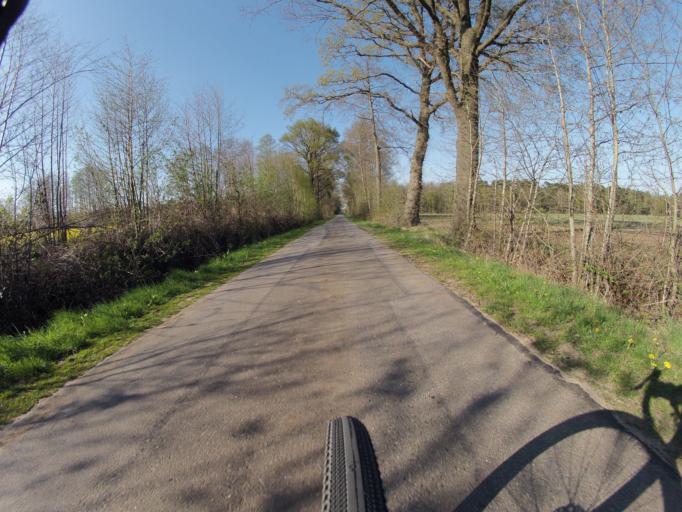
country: DE
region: Lower Saxony
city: Schuttorf
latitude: 52.3572
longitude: 7.2269
